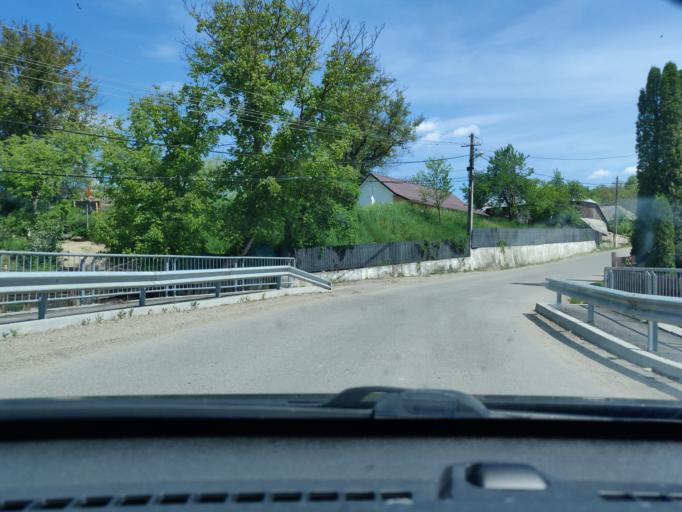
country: RO
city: Vizantea-Manastireasca
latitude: 45.9699
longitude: 26.8127
